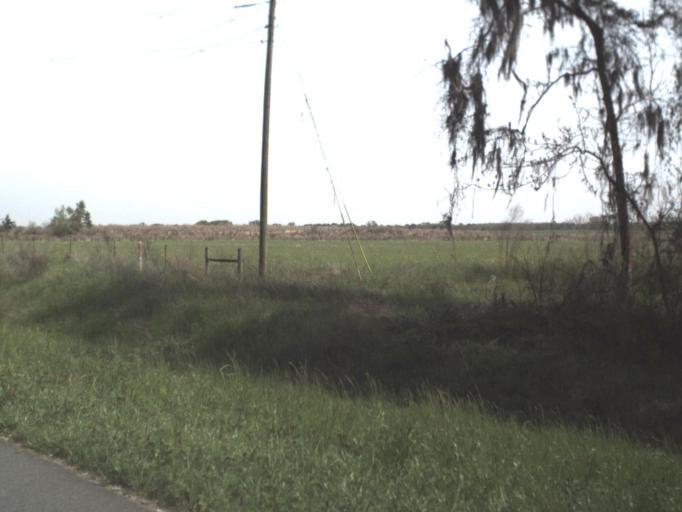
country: US
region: Florida
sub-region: Jackson County
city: Malone
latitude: 30.9476
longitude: -85.2570
